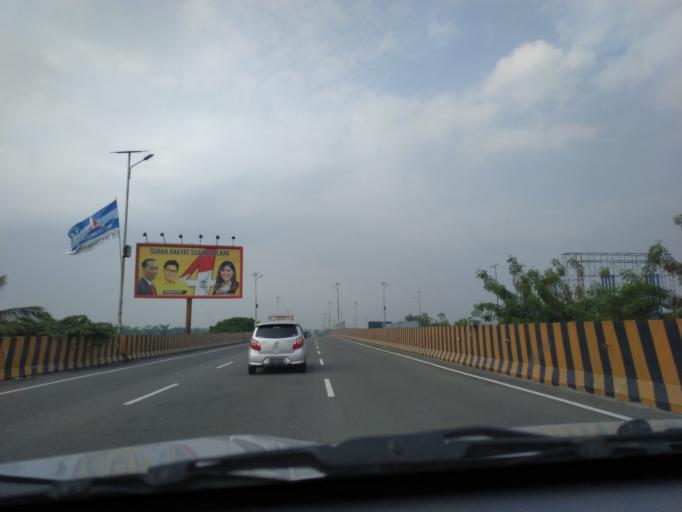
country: ID
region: North Sumatra
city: Percut
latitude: 3.6080
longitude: 98.8520
